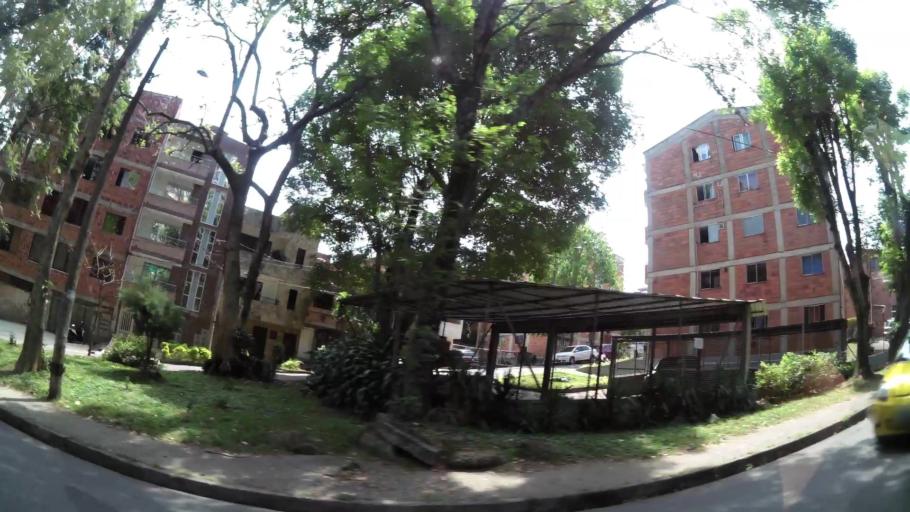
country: CO
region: Antioquia
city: Bello
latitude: 6.3198
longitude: -75.5659
